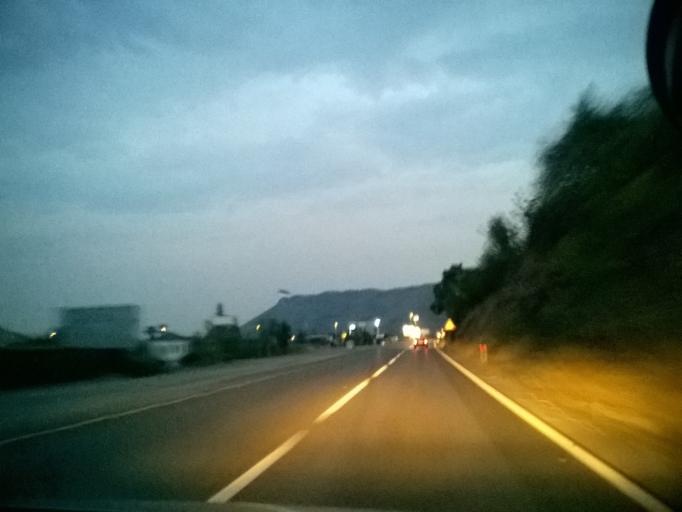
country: ME
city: Spuz
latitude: 42.4737
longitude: 19.1723
